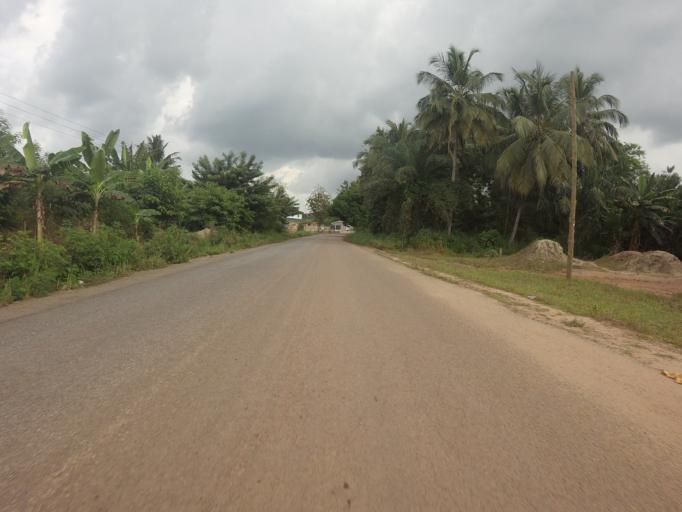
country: GH
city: Akropong
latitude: 5.9567
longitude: -0.1494
